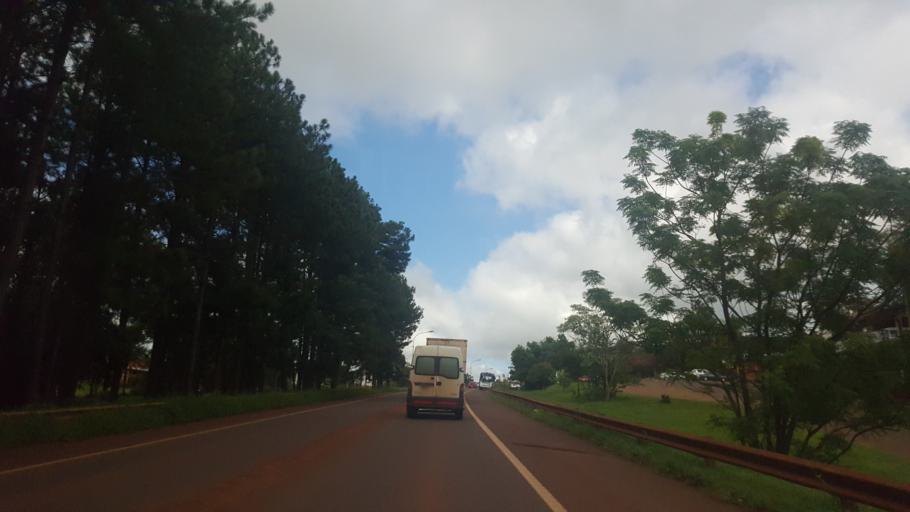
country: AR
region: Misiones
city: Aristobulo del Valle
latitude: -27.0849
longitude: -54.8270
